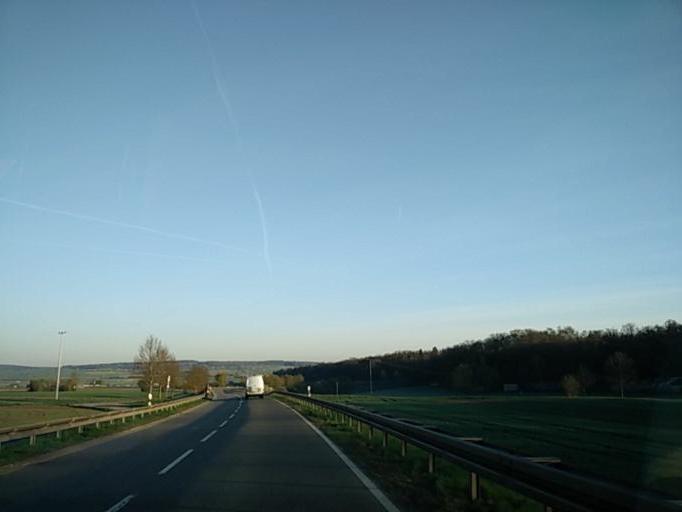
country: DE
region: Baden-Wuerttemberg
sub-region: Regierungsbezirk Stuttgart
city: Ehningen
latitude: 48.6382
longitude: 8.9465
